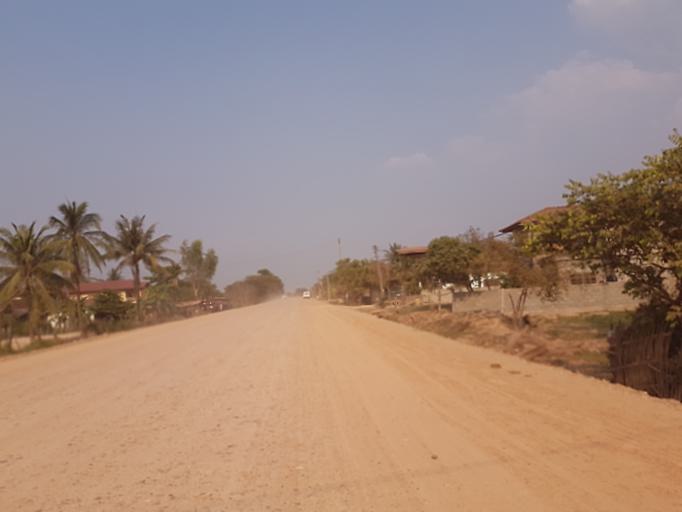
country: TH
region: Nong Khai
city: Nong Khai
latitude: 17.9850
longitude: 102.8941
